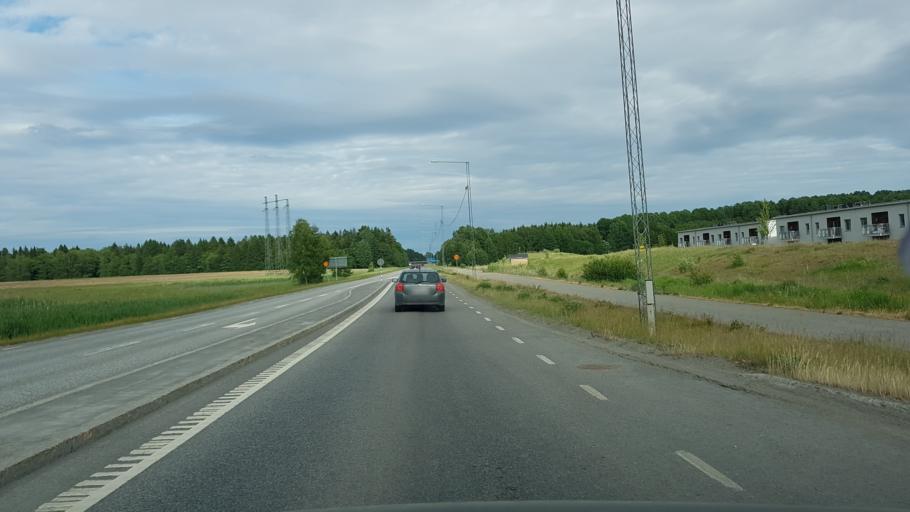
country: SE
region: Stockholm
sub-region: Haninge Kommun
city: Jordbro
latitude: 59.1222
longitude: 18.1149
